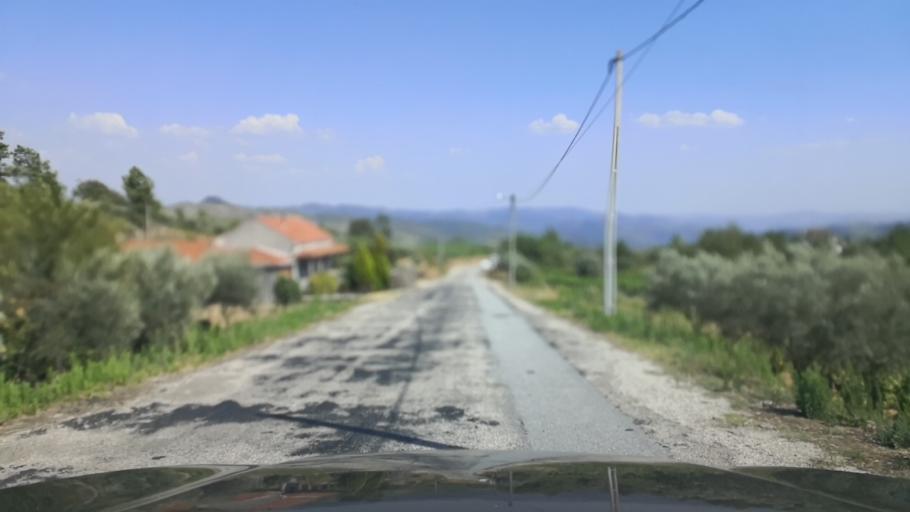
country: PT
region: Vila Real
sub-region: Sabrosa
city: Sabrosa
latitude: 41.2968
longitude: -7.4823
